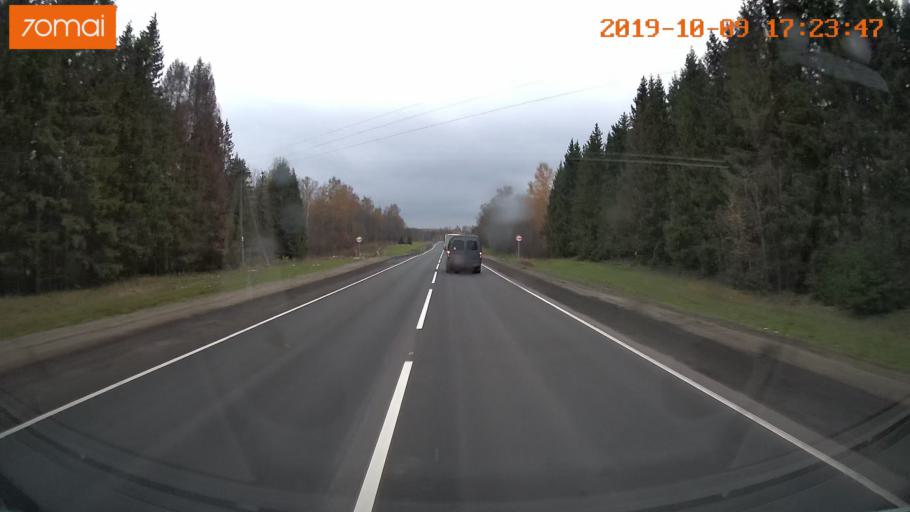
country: RU
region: Ivanovo
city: Furmanov
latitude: 57.1916
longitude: 41.1137
